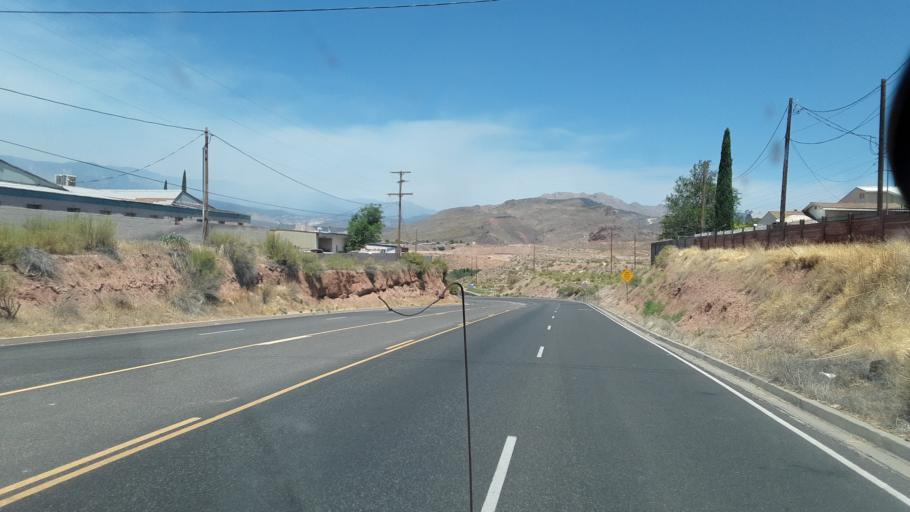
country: US
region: Utah
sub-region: Washington County
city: LaVerkin
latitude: 37.2139
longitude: -113.2729
